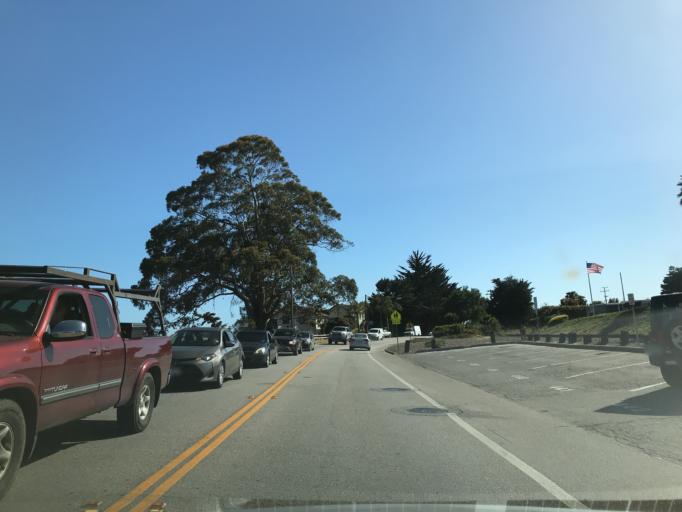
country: US
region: California
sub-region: Santa Cruz County
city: Capitola
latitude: 36.9697
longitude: -121.9560
